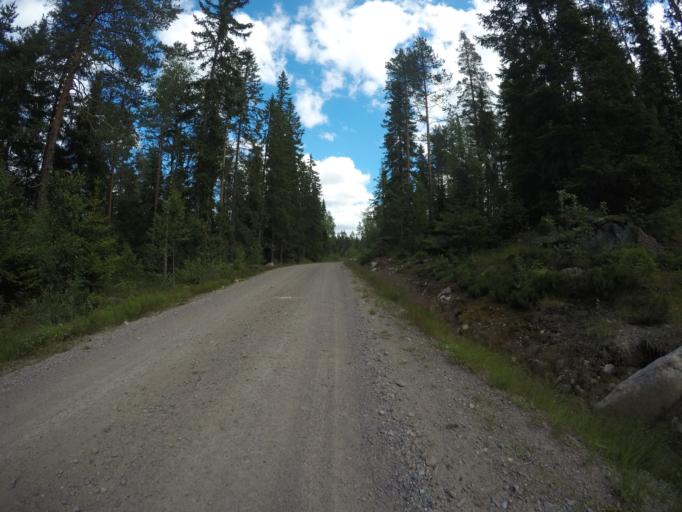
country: SE
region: OErebro
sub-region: Hallefors Kommun
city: Haellefors
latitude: 60.0683
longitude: 14.4805
